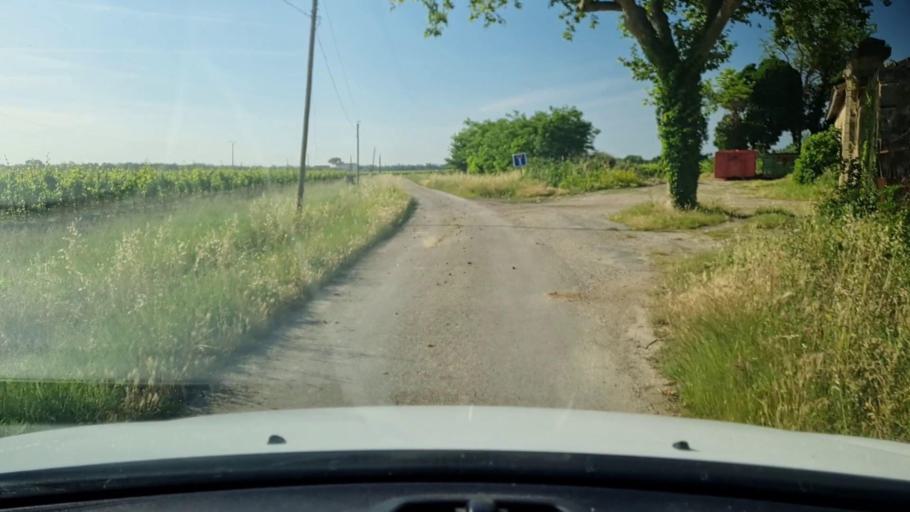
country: FR
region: Languedoc-Roussillon
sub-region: Departement du Gard
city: Le Cailar
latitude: 43.6438
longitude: 4.2252
